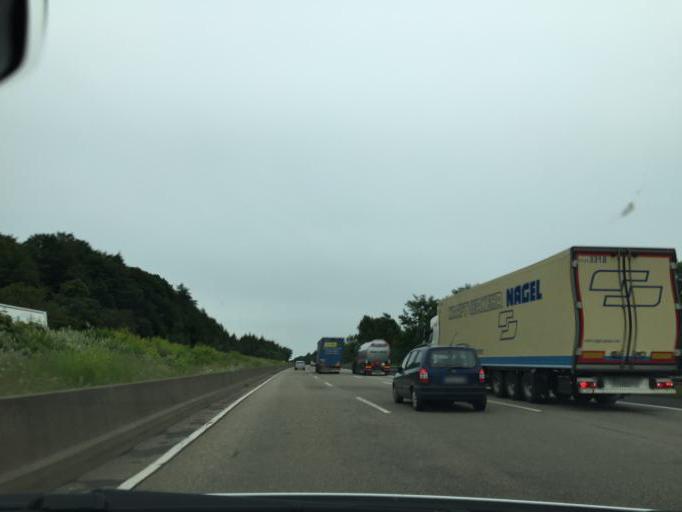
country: DE
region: Bavaria
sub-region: Regierungsbezirk Unterfranken
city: Motten
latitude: 50.3809
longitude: 9.7341
